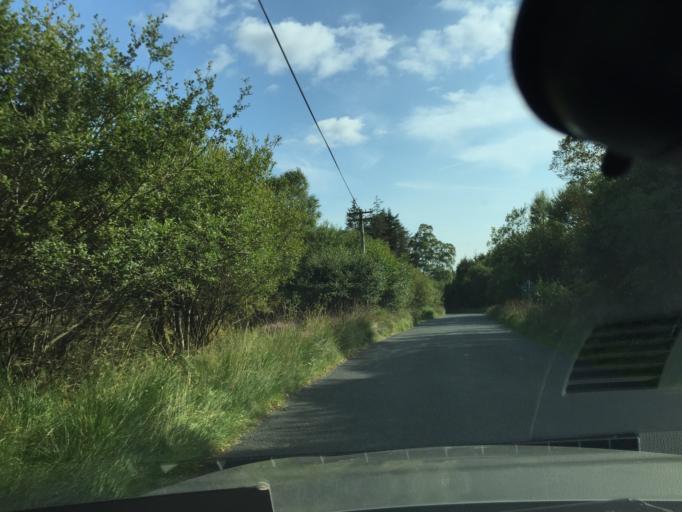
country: IE
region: Leinster
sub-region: Wicklow
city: Rathdrum
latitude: 53.0183
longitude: -6.3028
